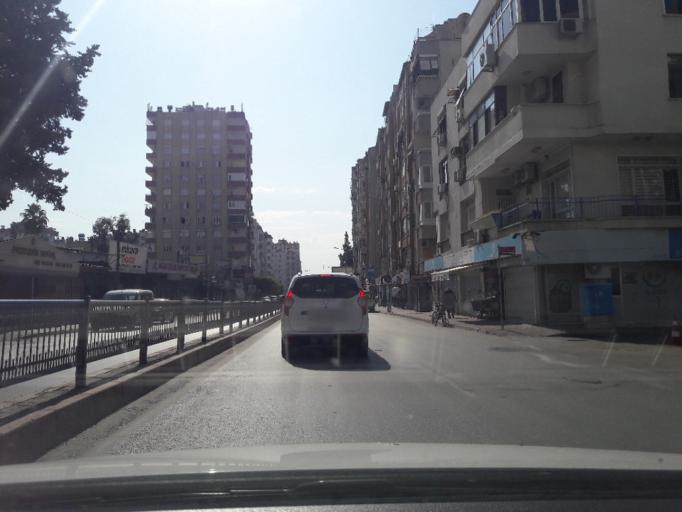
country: TR
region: Adana
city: Adana
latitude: 37.0116
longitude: 35.3231
